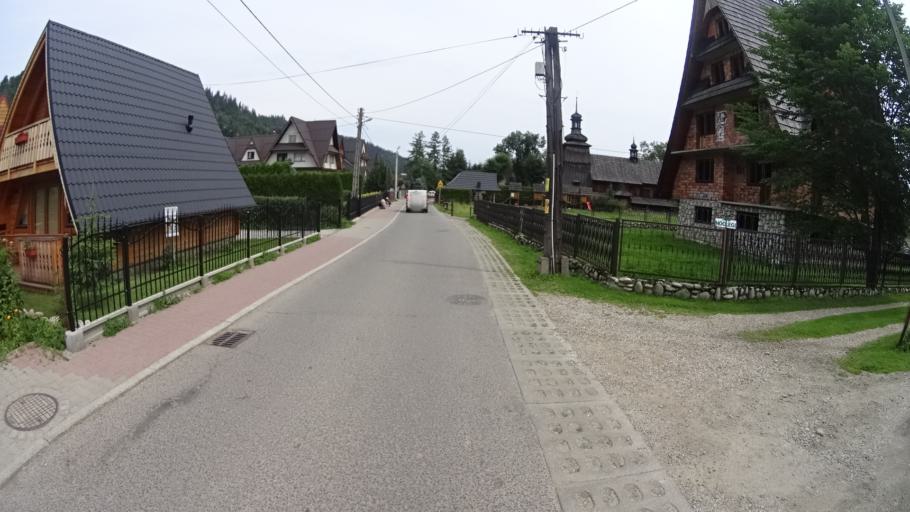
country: PL
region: Lesser Poland Voivodeship
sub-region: Powiat tatrzanski
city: Poronin
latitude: 49.3176
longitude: 19.9778
